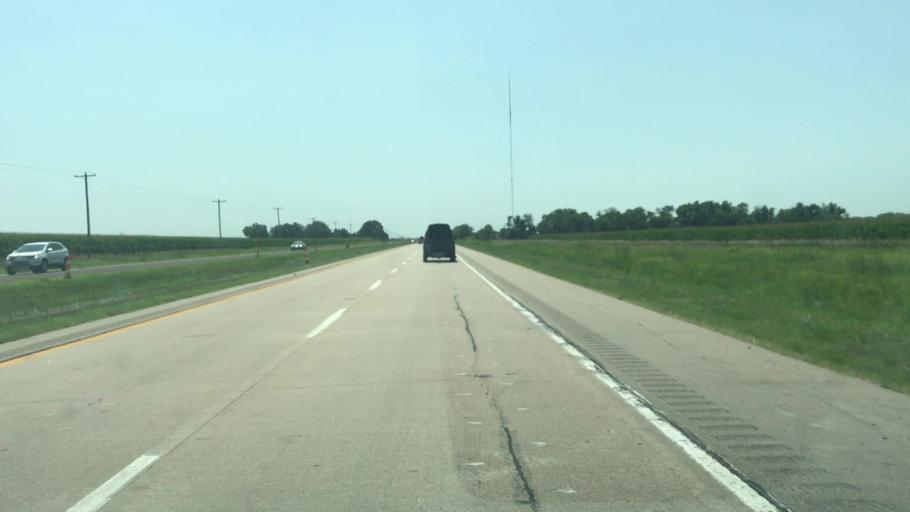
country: US
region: Nebraska
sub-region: Adams County
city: Hastings
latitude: 40.6605
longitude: -98.3824
